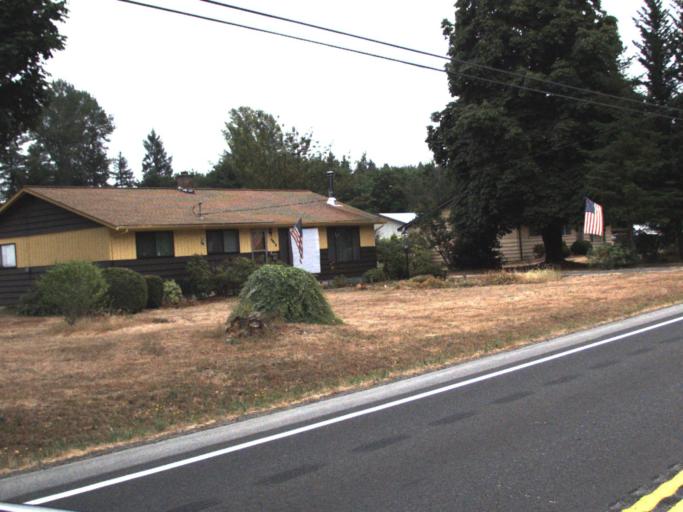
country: US
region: Washington
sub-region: King County
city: Carnation
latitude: 47.6267
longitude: -121.9103
